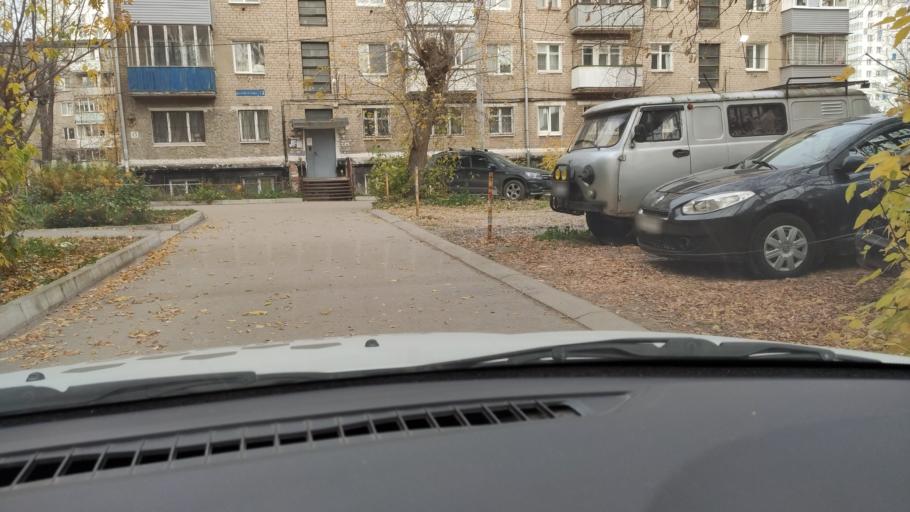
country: RU
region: Perm
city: Perm
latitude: 57.9884
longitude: 56.2636
